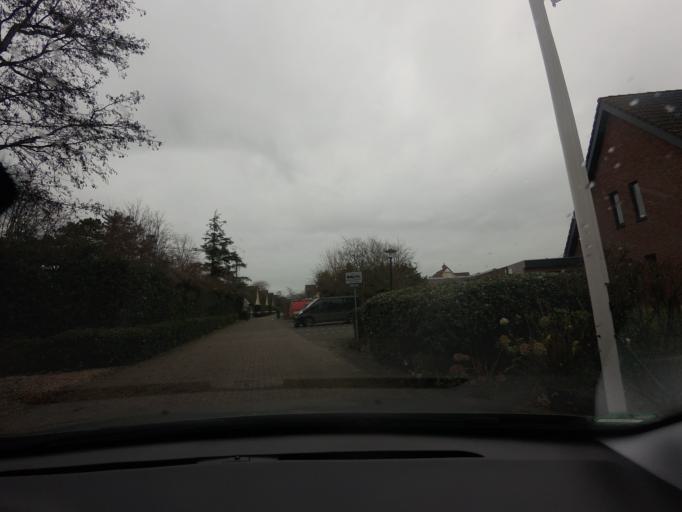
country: NL
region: North Holland
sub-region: Gemeente Texel
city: Den Burg
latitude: 53.0952
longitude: 4.7583
